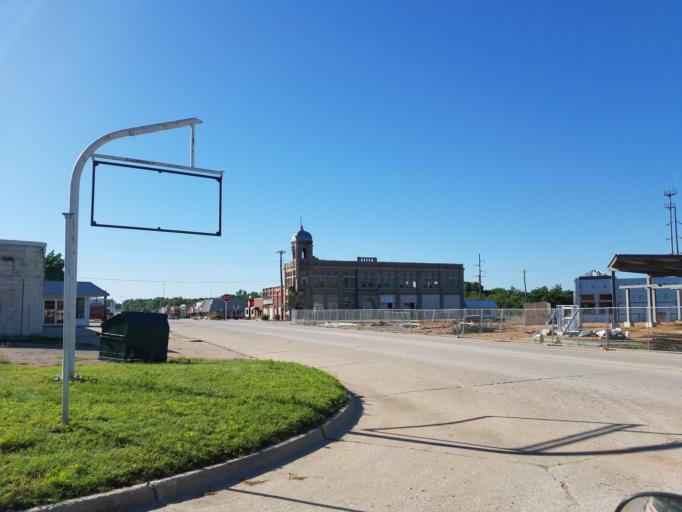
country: US
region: Oklahoma
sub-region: Johnston County
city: Tishomingo
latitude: 34.2372
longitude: -96.6818
